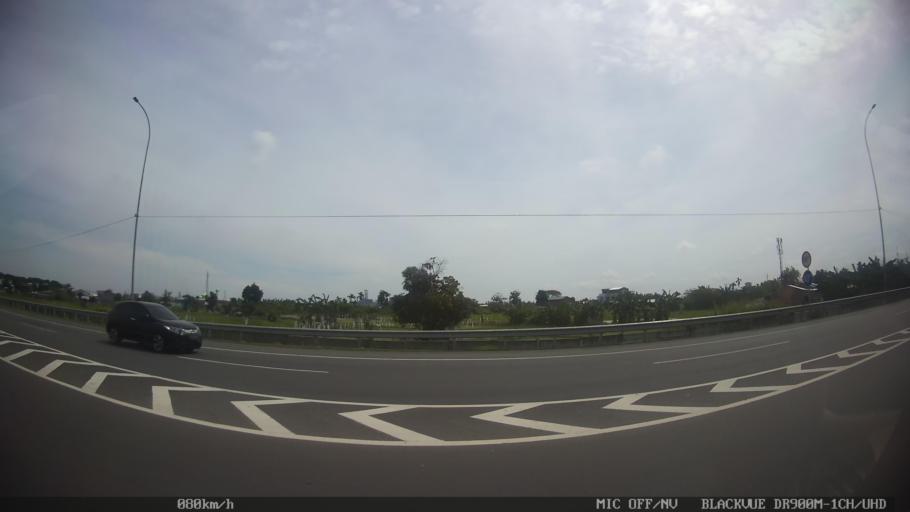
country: ID
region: North Sumatra
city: Medan
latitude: 3.6476
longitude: 98.6851
